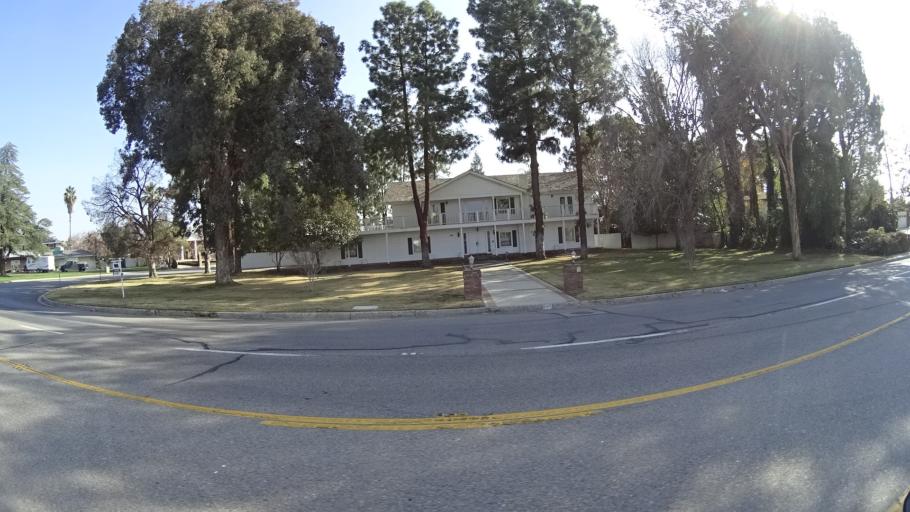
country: US
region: California
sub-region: Kern County
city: Oildale
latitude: 35.4066
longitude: -118.9949
